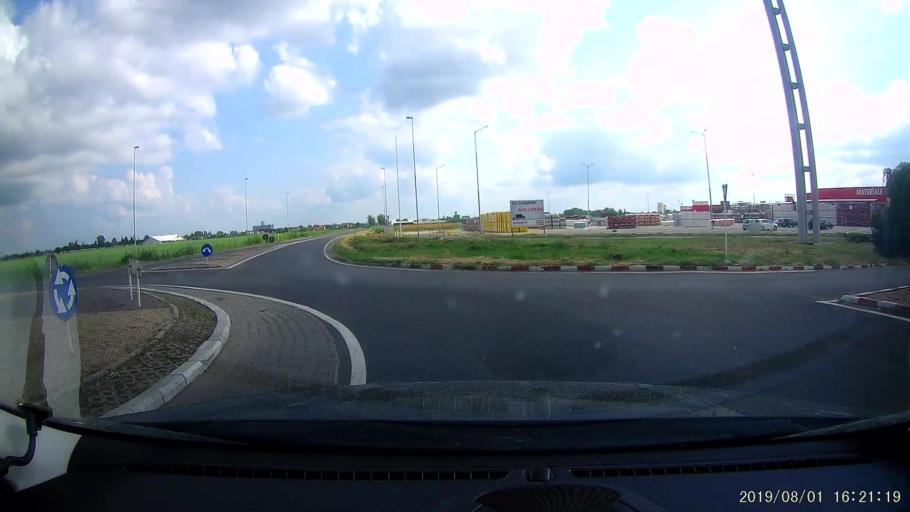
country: RO
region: Calarasi
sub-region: Municipiul Calarasi
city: Calarasi
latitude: 44.2189
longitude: 27.3401
